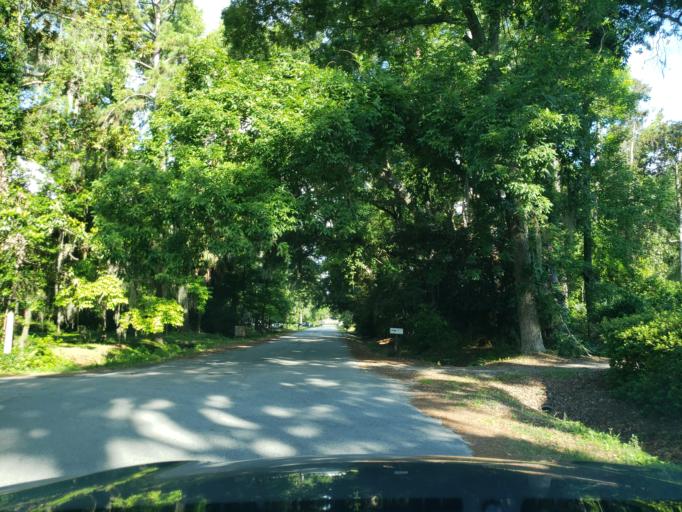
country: US
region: Georgia
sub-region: Chatham County
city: Isle of Hope
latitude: 31.9770
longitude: -81.0574
